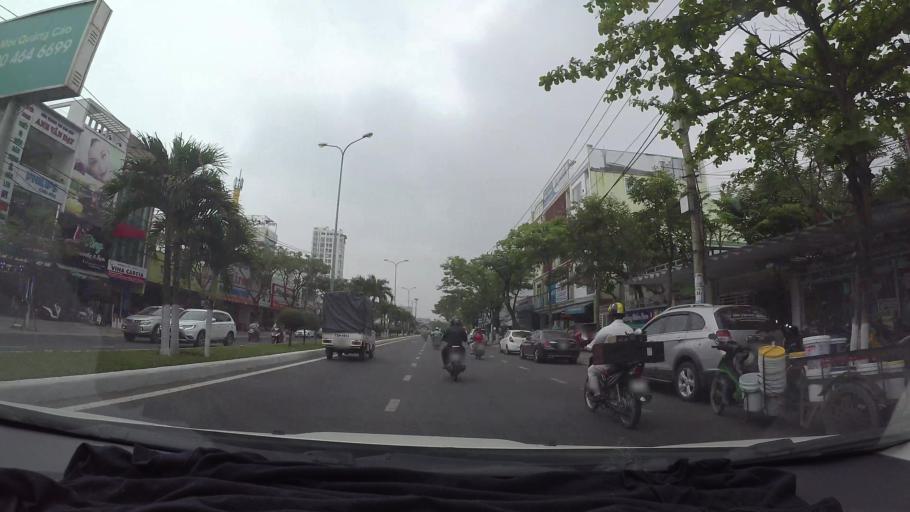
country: VN
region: Da Nang
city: Cam Le
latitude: 16.0373
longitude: 108.2102
